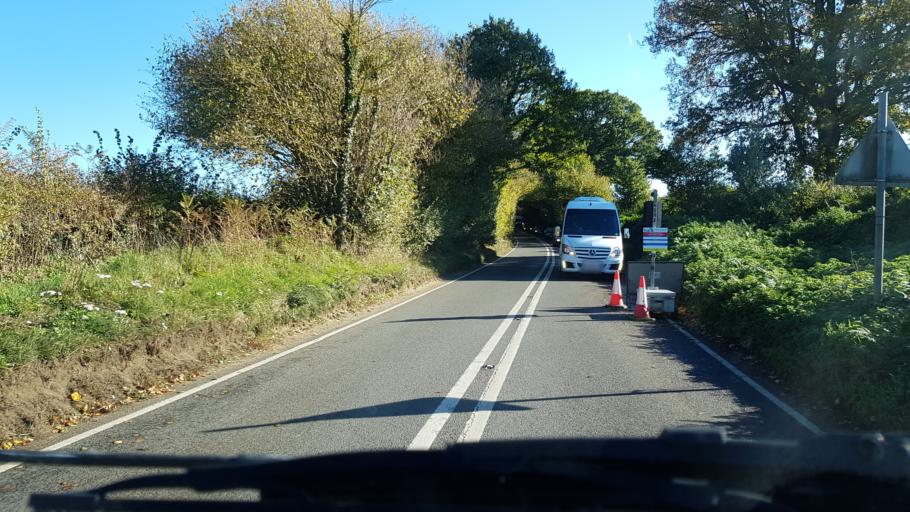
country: GB
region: England
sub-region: Surrey
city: East Horsley
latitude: 51.2149
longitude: -0.4125
